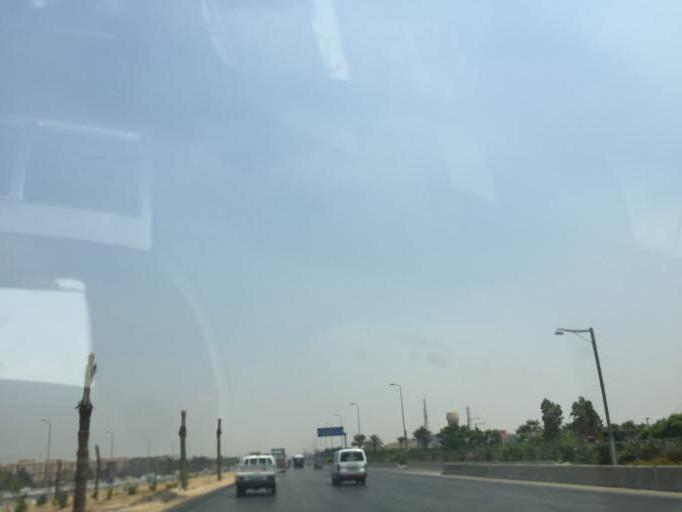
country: EG
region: Muhafazat al Qahirah
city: Cairo
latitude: 30.0321
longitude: 31.4038
